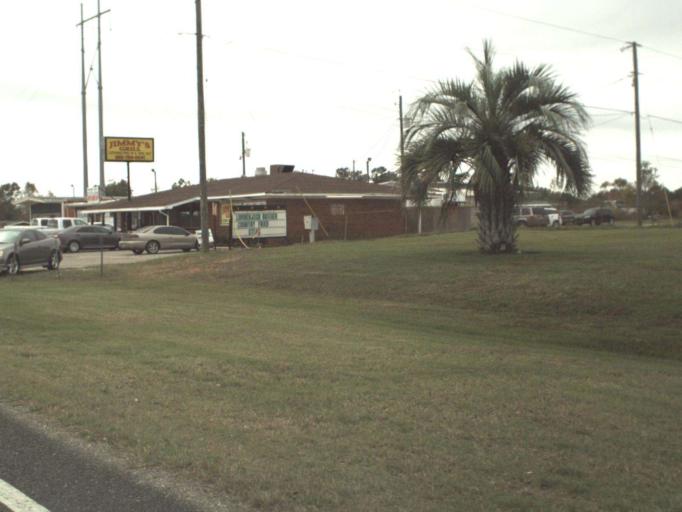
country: US
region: Florida
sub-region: Escambia County
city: Molino
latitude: 30.7017
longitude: -87.3505
